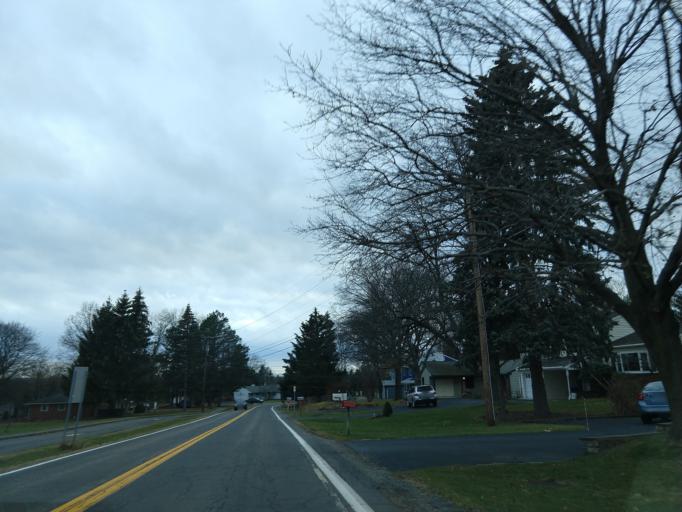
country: US
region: New York
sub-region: Tompkins County
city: Northeast Ithaca
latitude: 42.4740
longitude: -76.4695
